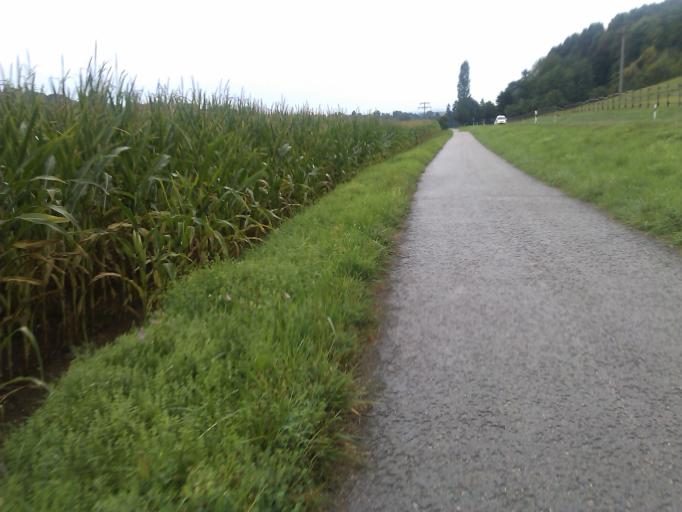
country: DE
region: Baden-Wuerttemberg
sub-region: Regierungsbezirk Stuttgart
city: Neckartenzlingen
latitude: 48.5722
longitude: 9.2267
